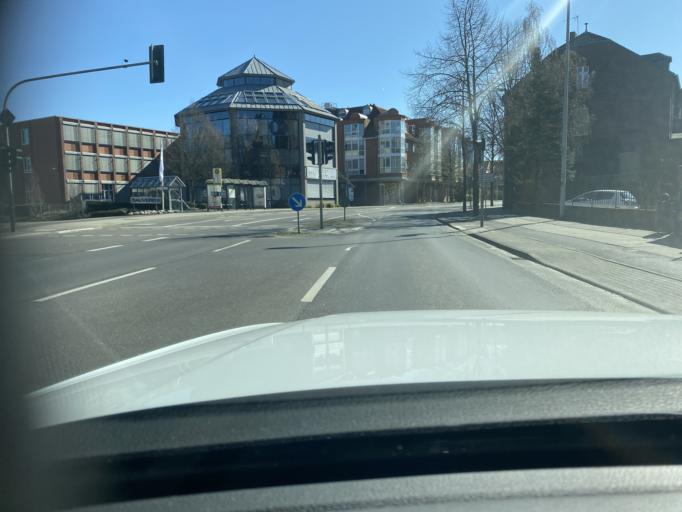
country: DE
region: North Rhine-Westphalia
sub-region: Regierungsbezirk Dusseldorf
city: Grevenbroich
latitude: 51.0892
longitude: 6.5906
